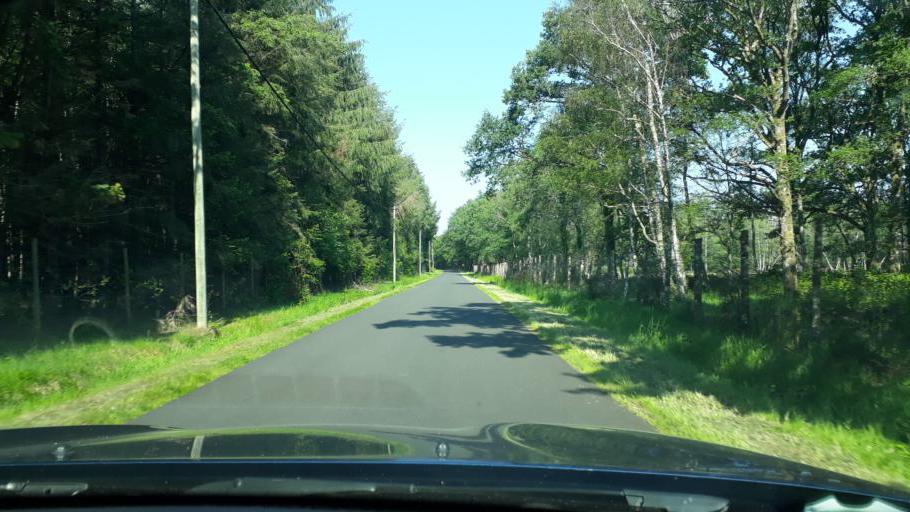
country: FR
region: Centre
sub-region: Departement du Loir-et-Cher
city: Dhuizon
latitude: 47.6240
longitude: 1.7190
